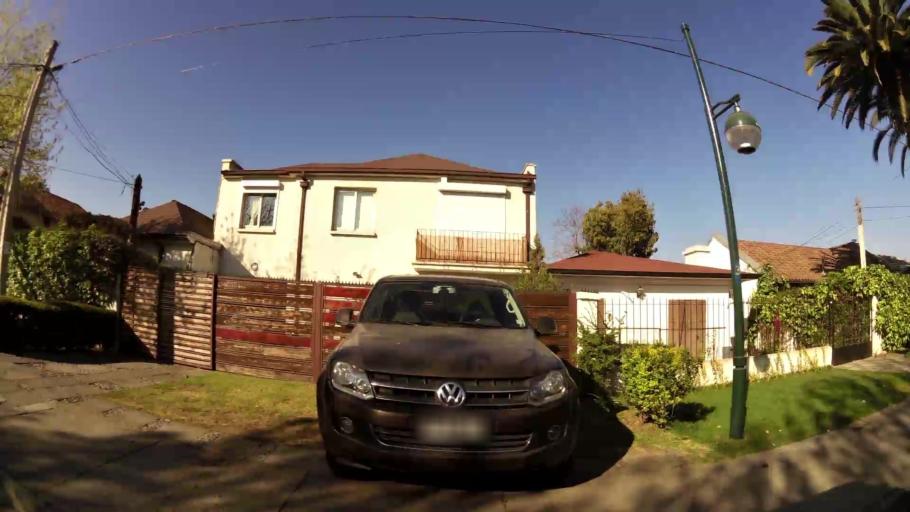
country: CL
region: Santiago Metropolitan
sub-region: Provincia de Santiago
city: Villa Presidente Frei, Nunoa, Santiago, Chile
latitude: -33.4423
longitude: -70.5872
